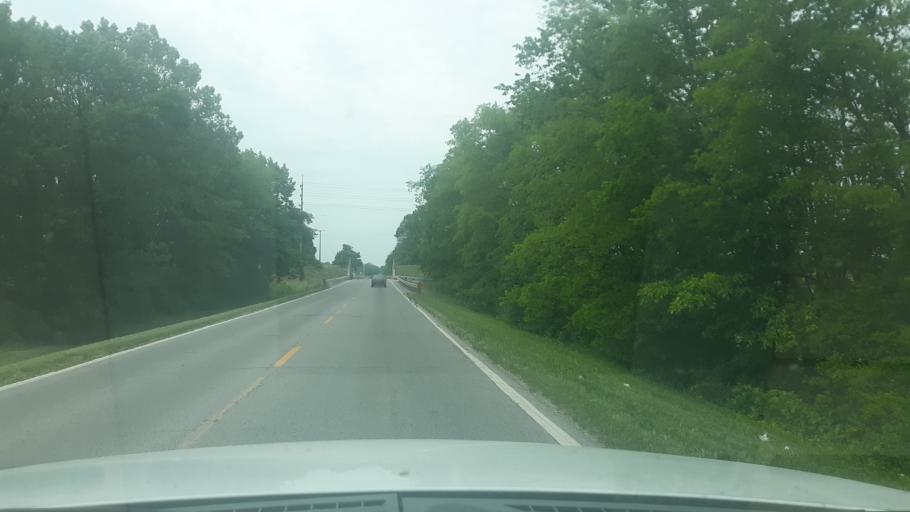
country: US
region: Illinois
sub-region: Saline County
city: Harrisburg
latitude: 37.7513
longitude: -88.5402
